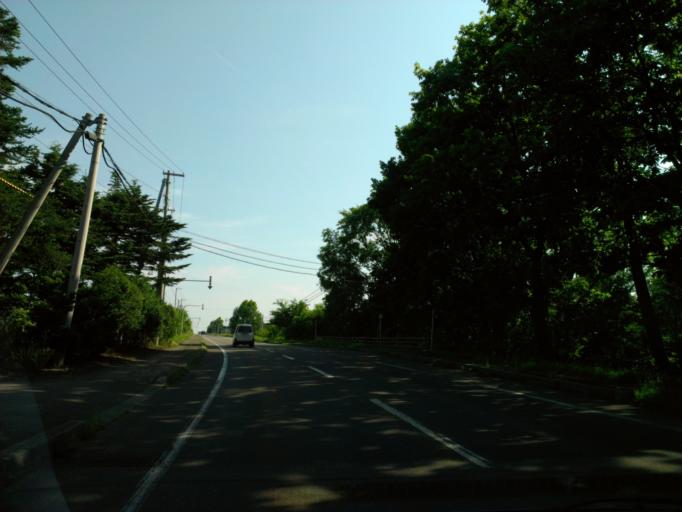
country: JP
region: Hokkaido
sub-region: Asahikawa-shi
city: Asahikawa
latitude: 43.6103
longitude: 142.4769
